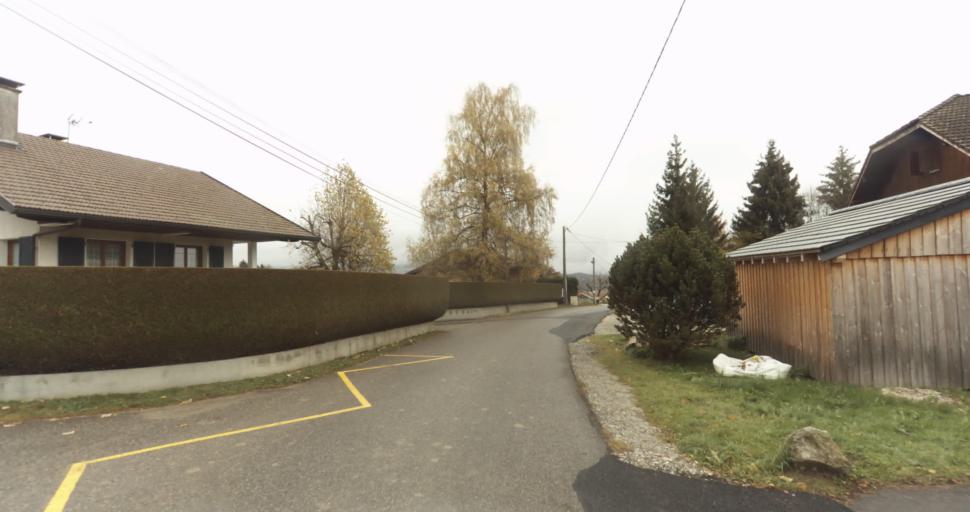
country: FR
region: Rhone-Alpes
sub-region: Departement de la Haute-Savoie
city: Groisy
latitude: 46.0301
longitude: 6.1961
